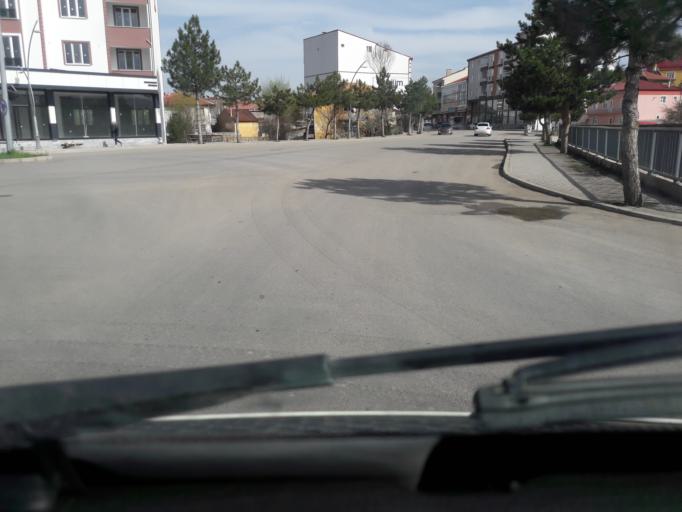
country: TR
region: Gumushane
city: Kelkit
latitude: 40.1354
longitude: 39.4337
